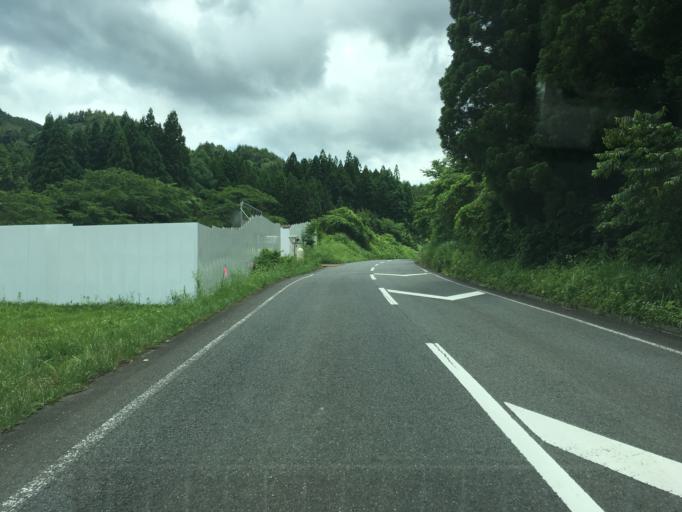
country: JP
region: Miyagi
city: Marumori
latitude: 37.7132
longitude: 140.8822
